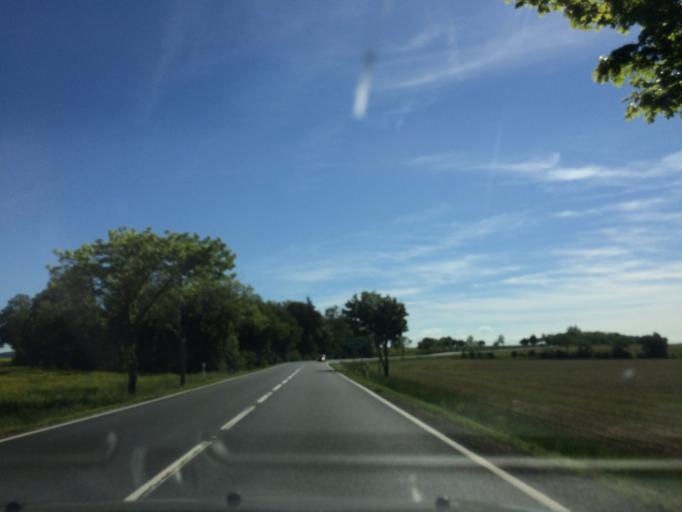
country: PL
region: Lower Silesian Voivodeship
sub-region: Powiat wroclawski
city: Sobotka
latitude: 50.9518
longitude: 16.7600
